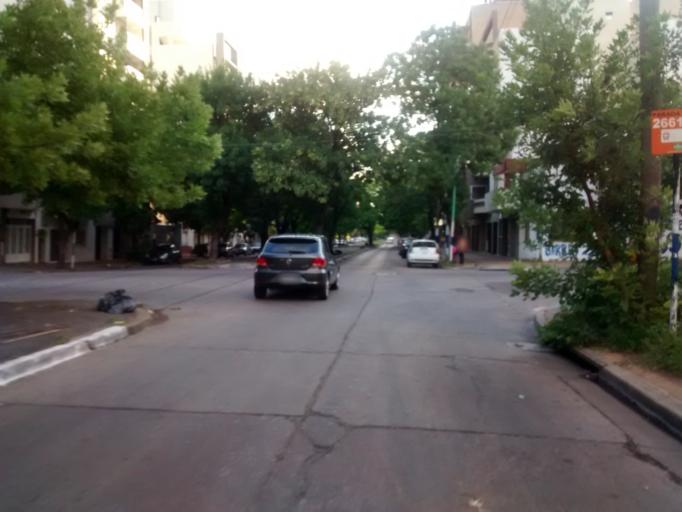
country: AR
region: Buenos Aires
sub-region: Partido de La Plata
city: La Plata
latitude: -34.9092
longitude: -57.9661
